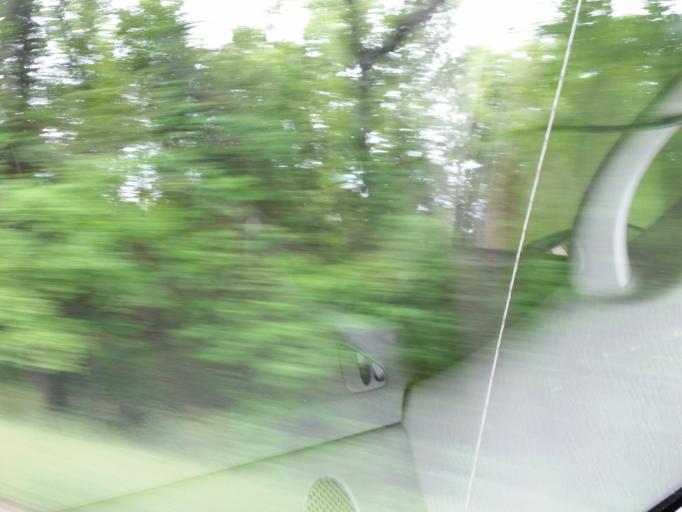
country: US
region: Georgia
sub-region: Peach County
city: Byron
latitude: 32.6650
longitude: -83.8295
